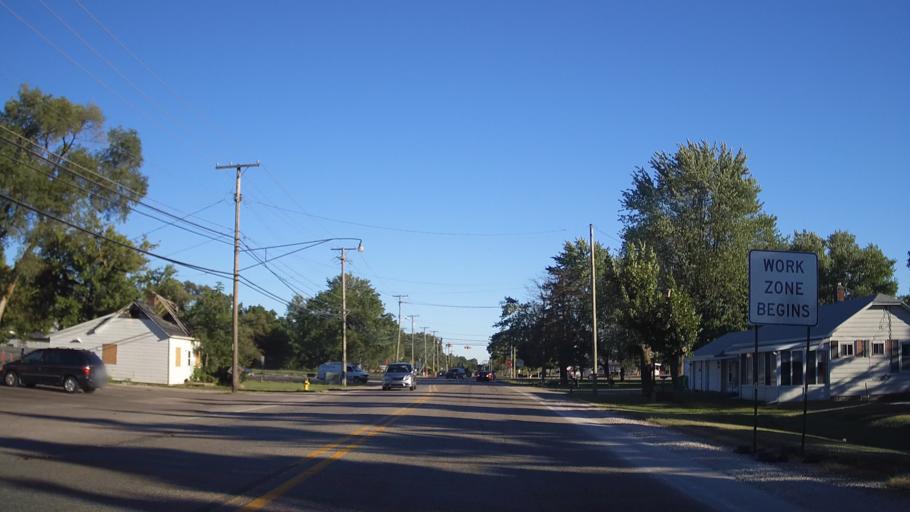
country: US
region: Michigan
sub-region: Macomb County
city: Shelby
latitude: 42.7020
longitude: -82.9591
